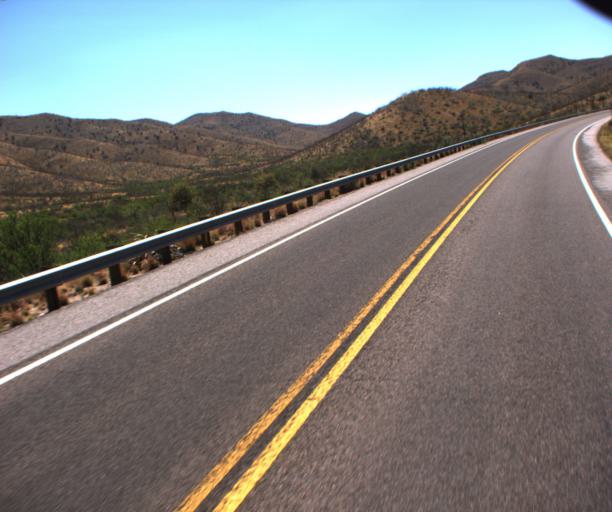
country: US
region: Arizona
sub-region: Cochise County
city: Bisbee
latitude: 31.4356
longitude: -109.8402
